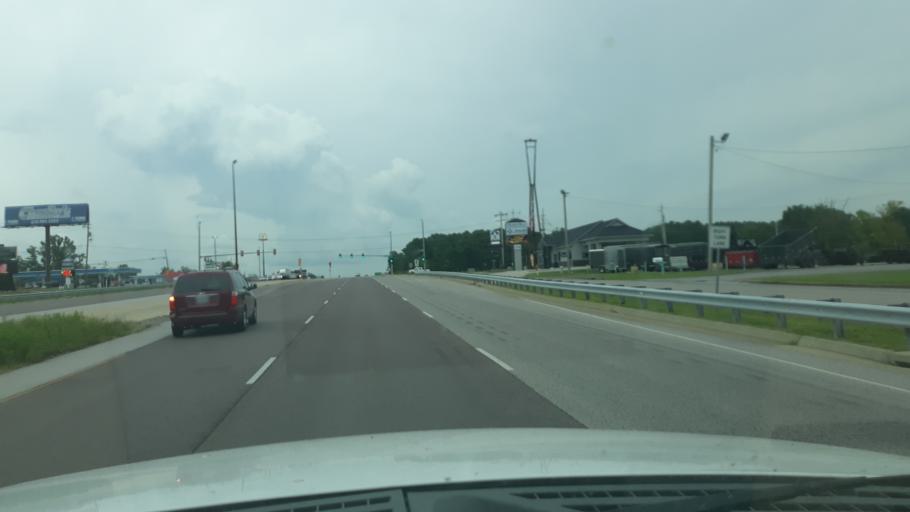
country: US
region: Illinois
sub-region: Williamson County
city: Crainville
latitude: 37.7450
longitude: -89.0799
